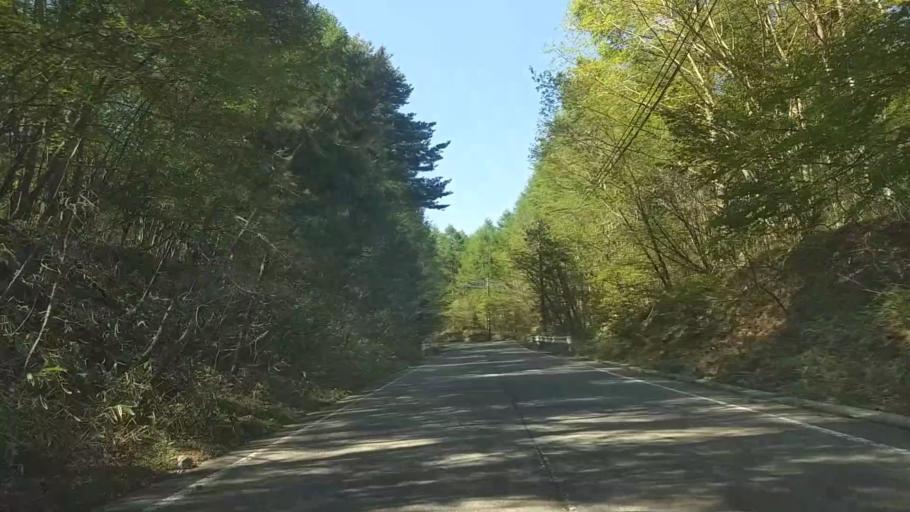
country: JP
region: Yamanashi
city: Nirasaki
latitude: 35.9173
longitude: 138.4045
